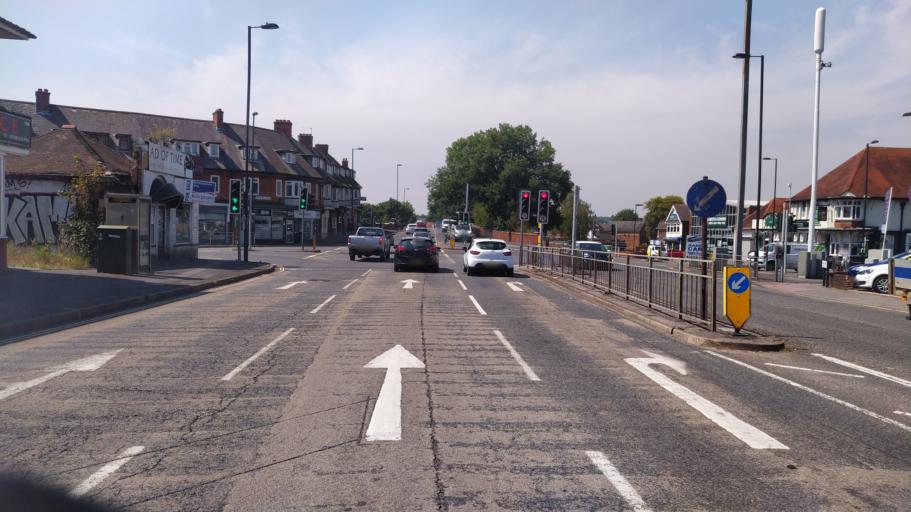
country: GB
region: England
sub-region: Southampton
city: Southampton
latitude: 50.9176
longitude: -1.3745
